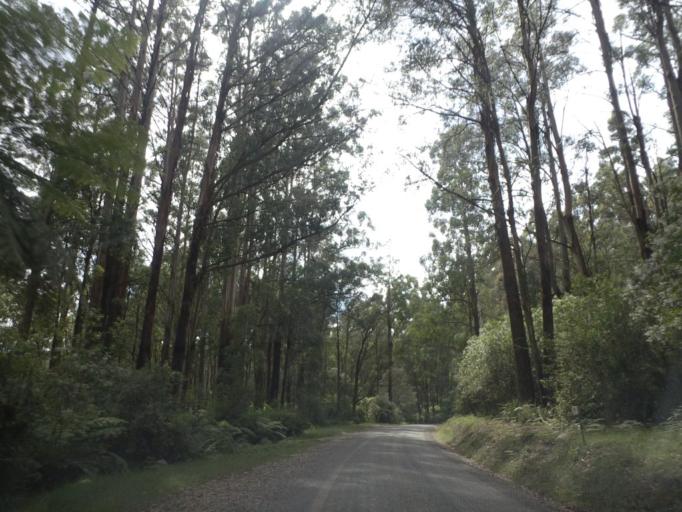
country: AU
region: Victoria
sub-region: Yarra Ranges
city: Healesville
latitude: -37.5082
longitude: 145.5154
